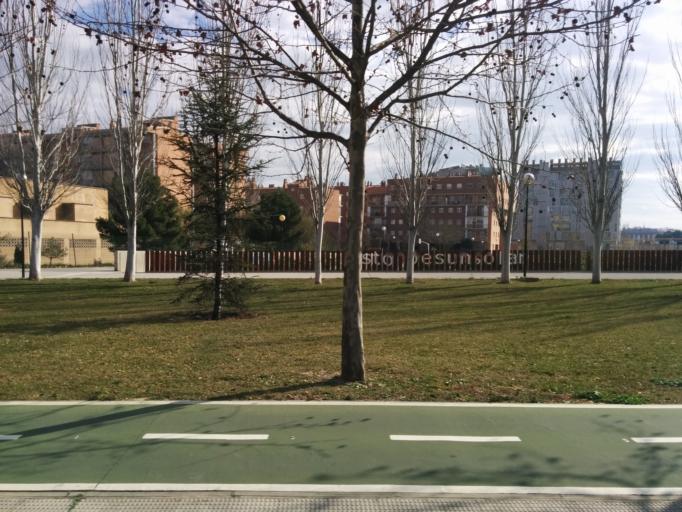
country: ES
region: Aragon
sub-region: Provincia de Zaragoza
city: Zaragoza
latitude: 41.6637
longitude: -0.8877
